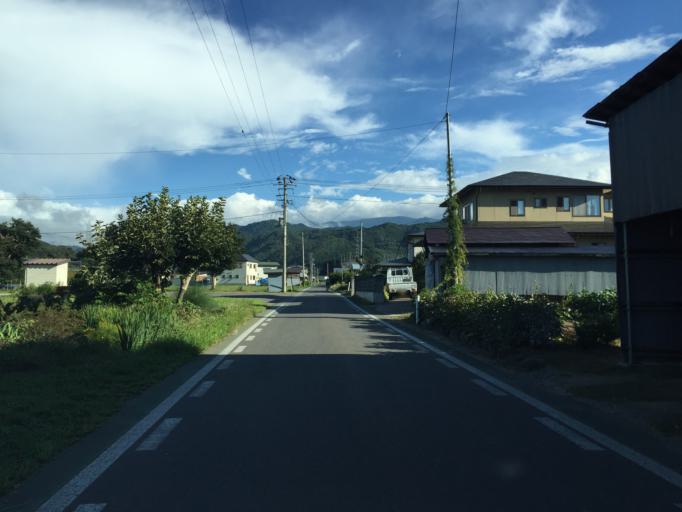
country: JP
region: Yamagata
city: Yonezawa
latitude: 37.8733
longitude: 140.1406
